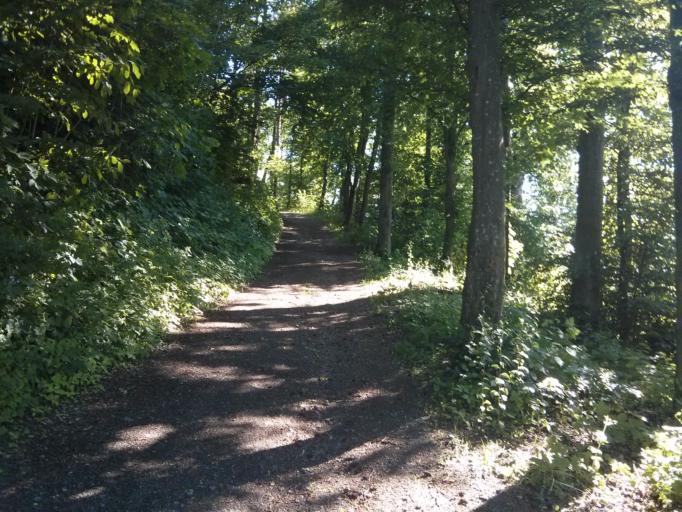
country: DE
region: Bavaria
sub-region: Lower Bavaria
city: Metten
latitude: 48.8268
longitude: 12.9099
